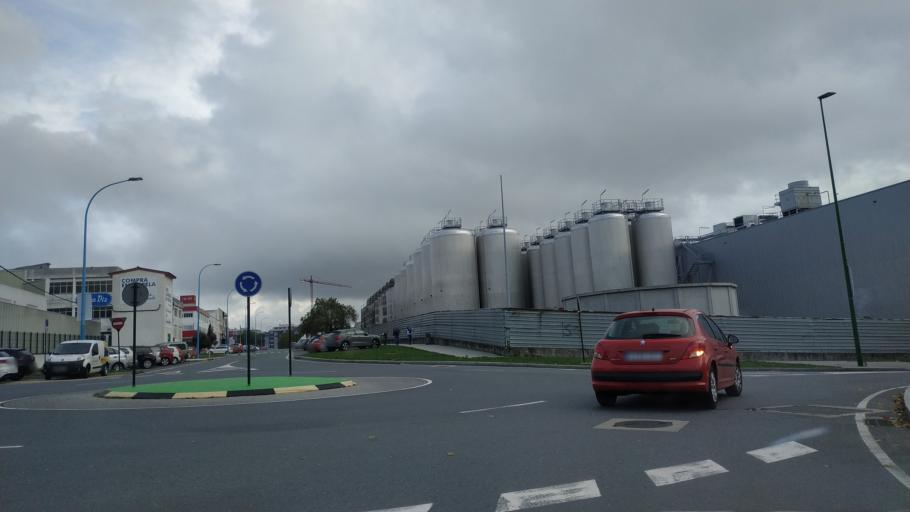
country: ES
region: Galicia
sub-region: Provincia da Coruna
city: A Coruna
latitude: 43.3544
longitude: -8.4220
